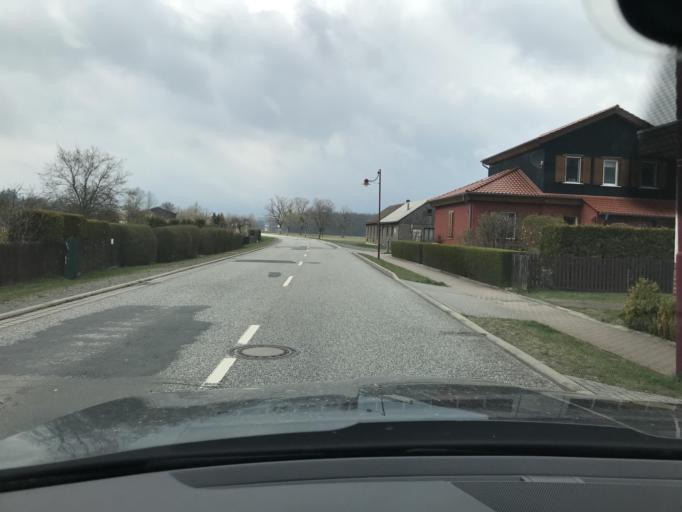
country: DE
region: Saxony-Anhalt
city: Harzgerode
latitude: 51.6500
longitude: 11.1396
